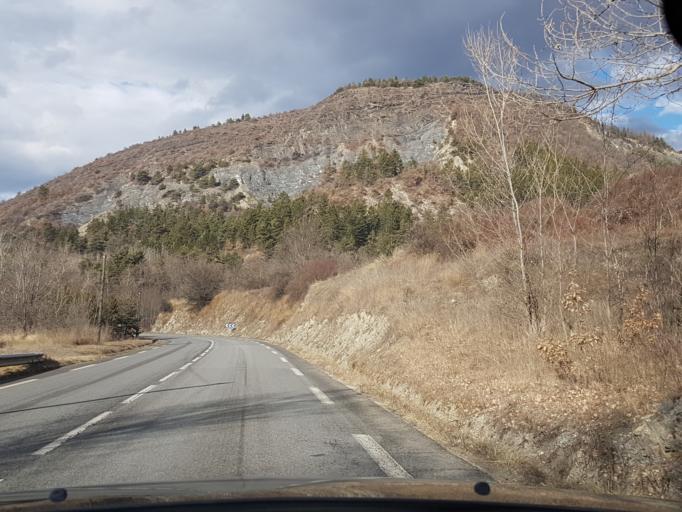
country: FR
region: Provence-Alpes-Cote d'Azur
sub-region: Departement des Hautes-Alpes
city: Tallard
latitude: 44.4757
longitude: 6.1219
